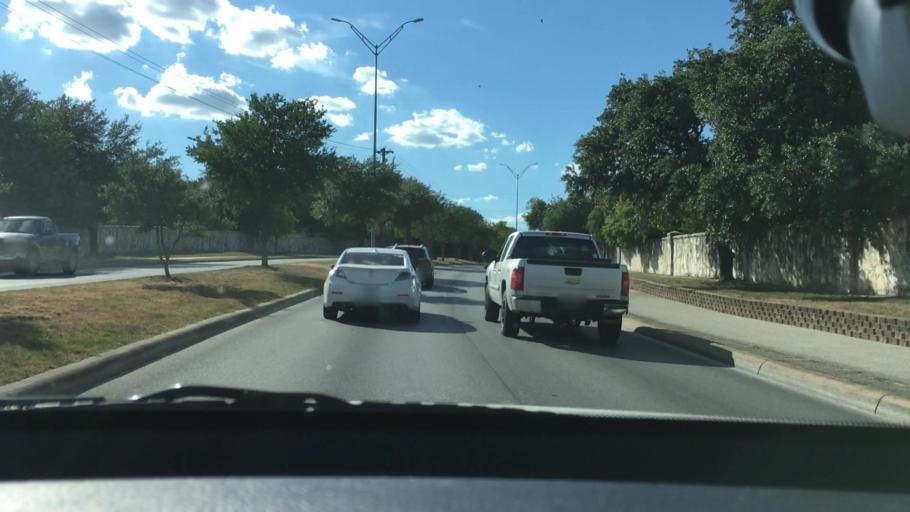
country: US
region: Texas
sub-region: Bexar County
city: Selma
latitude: 29.5837
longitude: -98.2854
